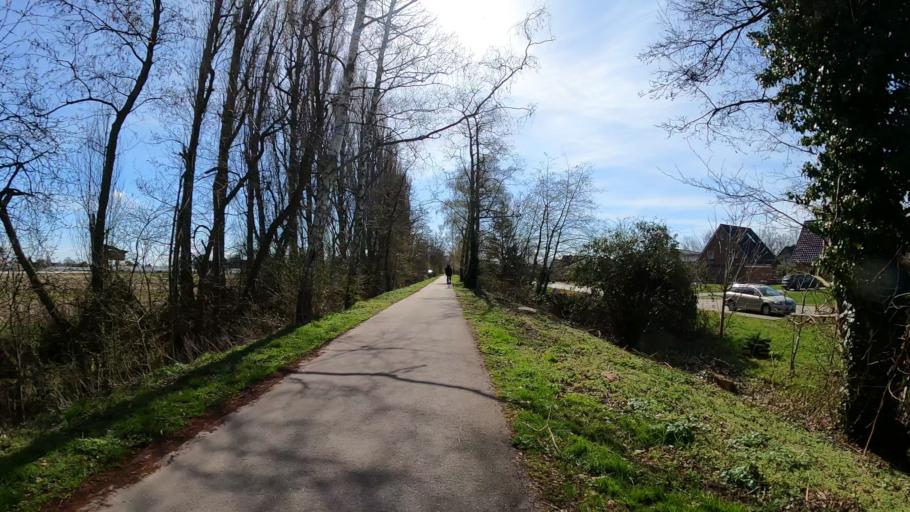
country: DE
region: Hamburg
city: Rothenburgsort
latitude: 53.4793
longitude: 10.0788
